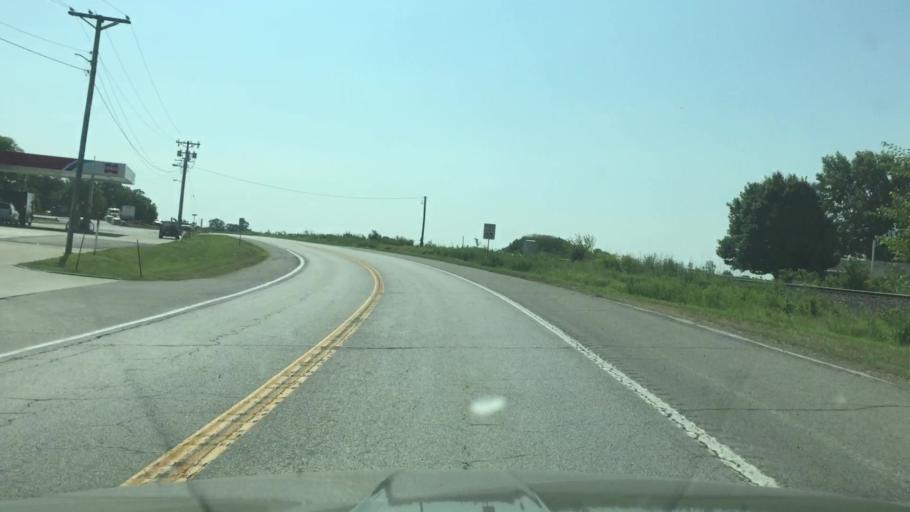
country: US
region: Missouri
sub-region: Pettis County
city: Sedalia
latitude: 38.6971
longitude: -93.1812
